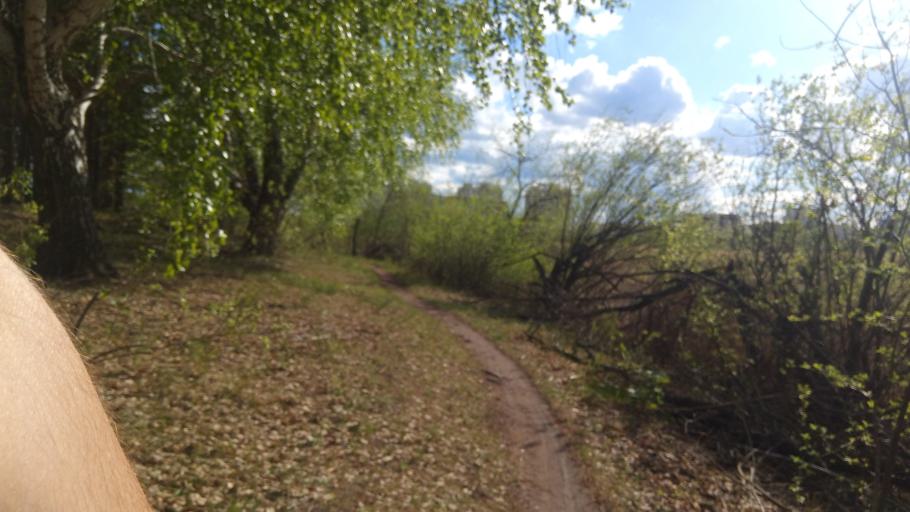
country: RU
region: Chelyabinsk
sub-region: Gorod Chelyabinsk
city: Chelyabinsk
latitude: 55.1634
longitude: 61.3132
